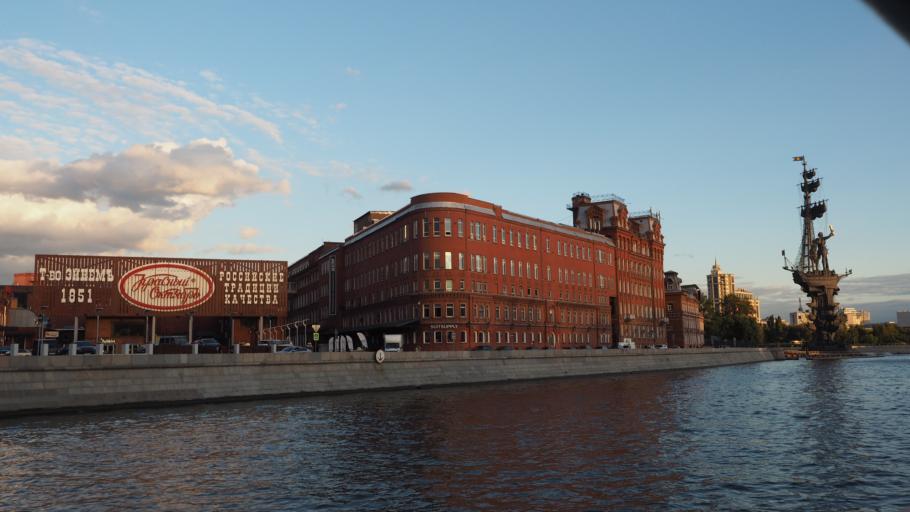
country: RU
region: Moscow
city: Moscow
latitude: 55.7424
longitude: 37.6079
